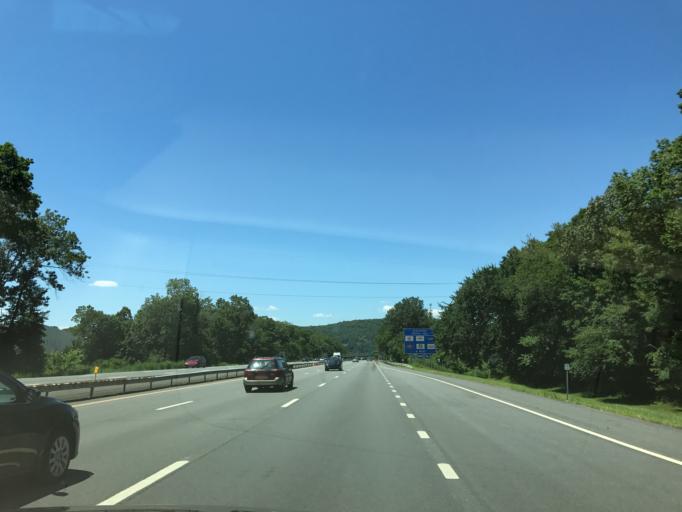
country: US
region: New York
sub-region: Rockland County
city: Montebello
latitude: 41.1184
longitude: -74.1209
